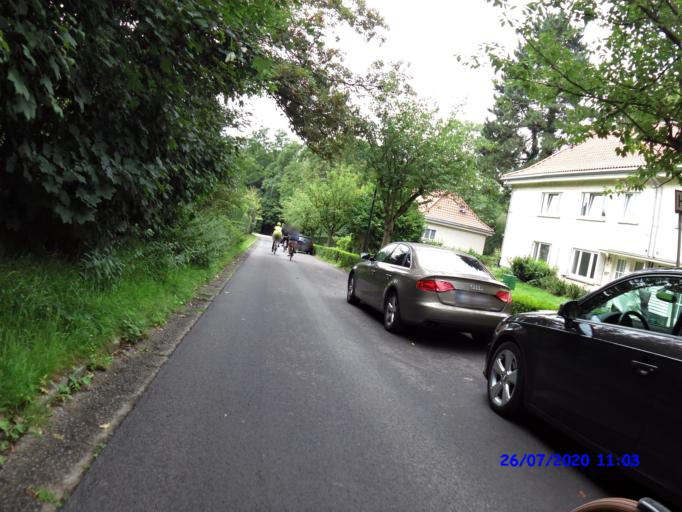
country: BE
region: Flanders
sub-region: Provincie Vlaams-Brabant
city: Linkebeek
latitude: 50.7774
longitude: 4.3479
